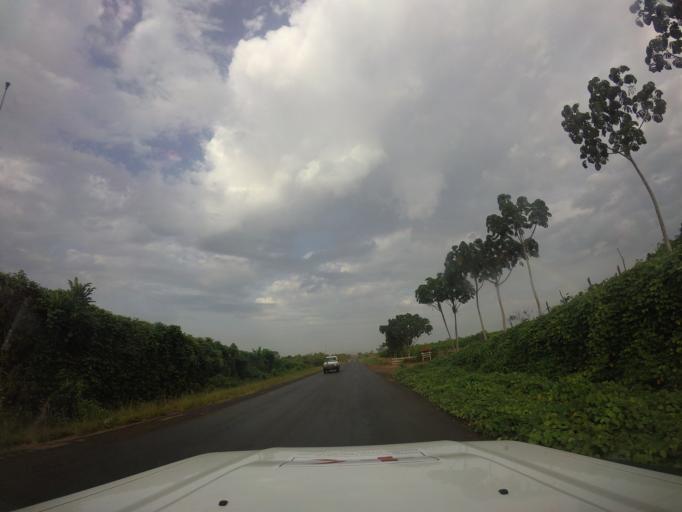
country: LR
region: Bomi
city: Tubmanburg
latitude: 6.7298
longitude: -11.0164
